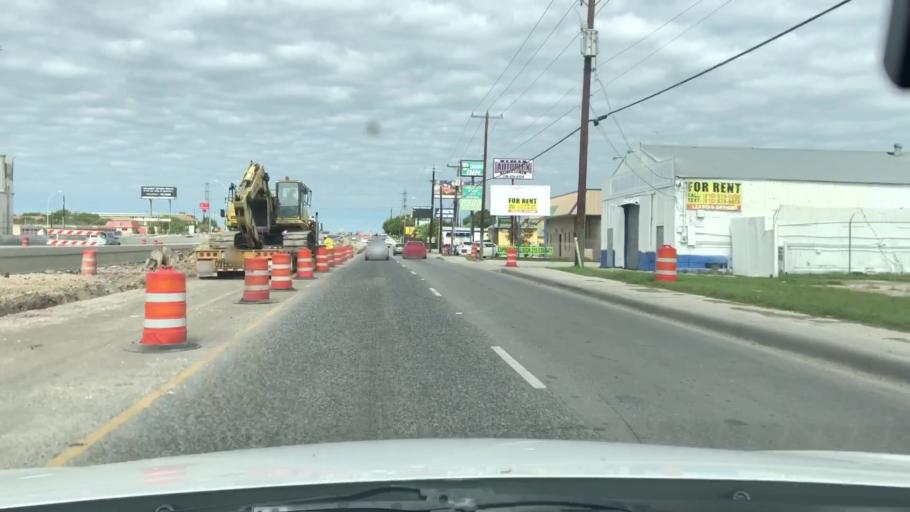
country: US
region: Texas
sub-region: Bexar County
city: Lackland Air Force Base
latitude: 29.4056
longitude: -98.6493
